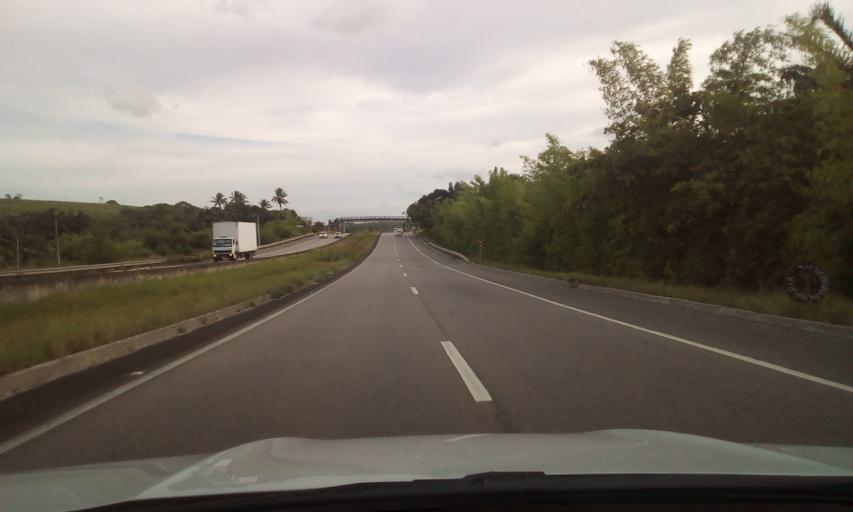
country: BR
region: Paraiba
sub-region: Alhandra
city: Alhandra
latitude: -7.3975
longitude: -34.9556
